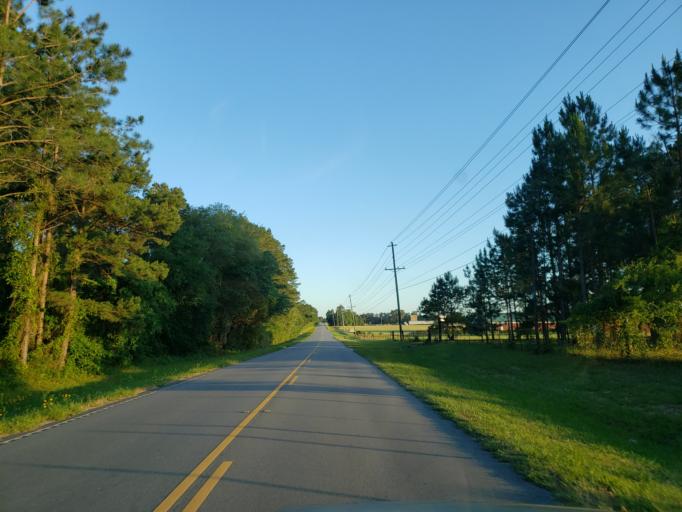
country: US
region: Georgia
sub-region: Lowndes County
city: Valdosta
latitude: 30.7039
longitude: -83.2411
